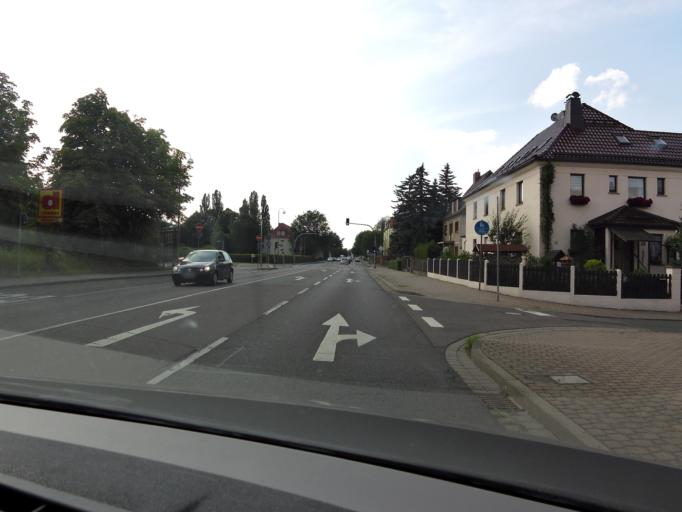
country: DE
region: Saxony
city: Grossposna
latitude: 51.2771
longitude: 12.4705
